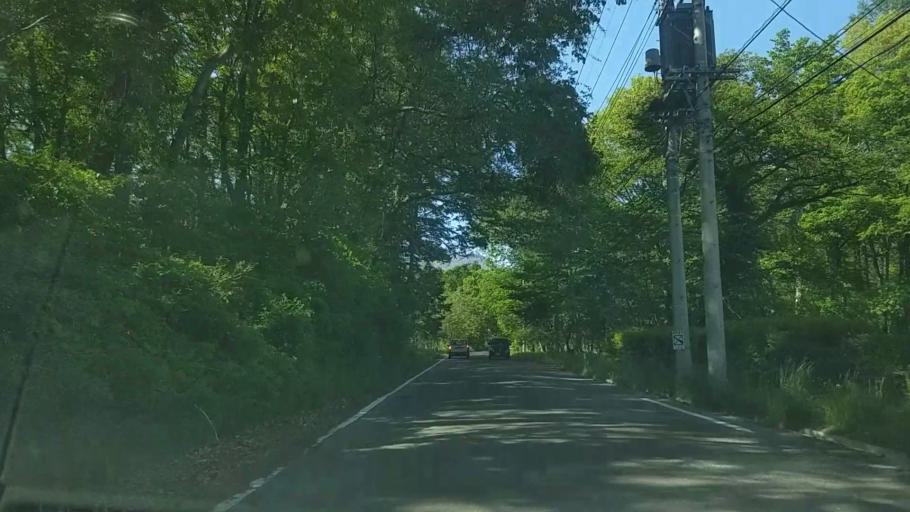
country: JP
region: Yamanashi
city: Nirasaki
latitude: 35.8834
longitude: 138.3565
